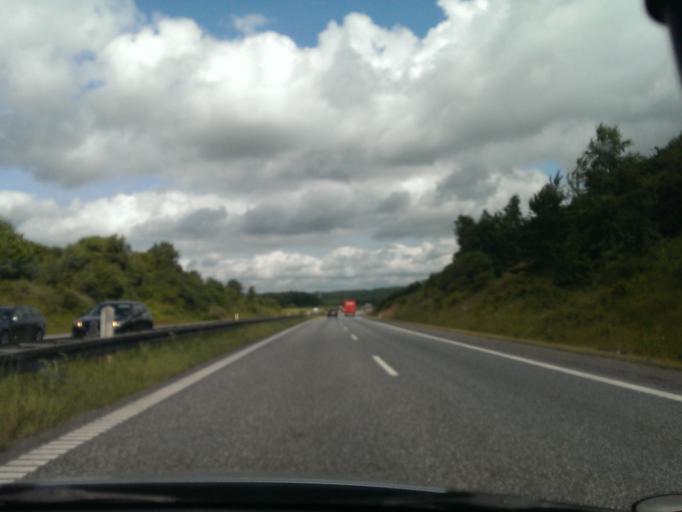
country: DK
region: North Denmark
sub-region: Mariagerfjord Kommune
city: Hobro
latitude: 56.6061
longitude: 9.7451
